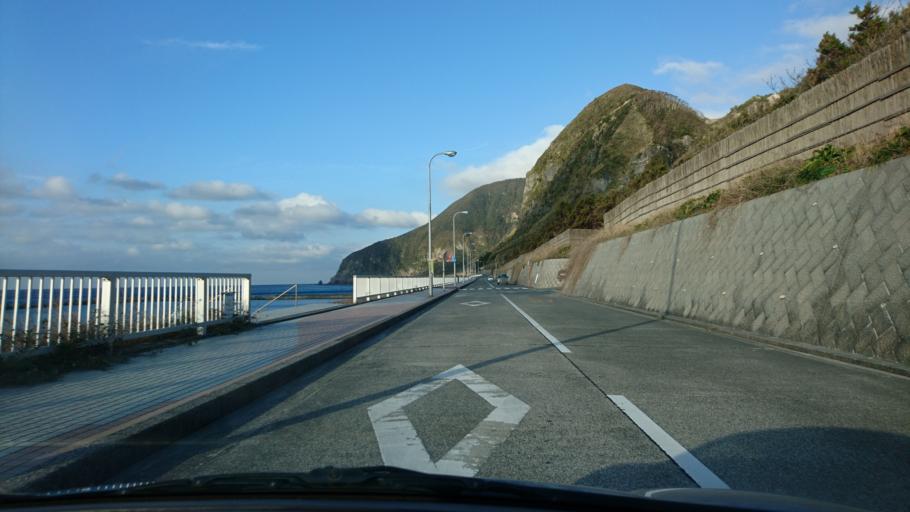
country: JP
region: Shizuoka
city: Shimoda
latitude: 34.3803
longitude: 139.2546
